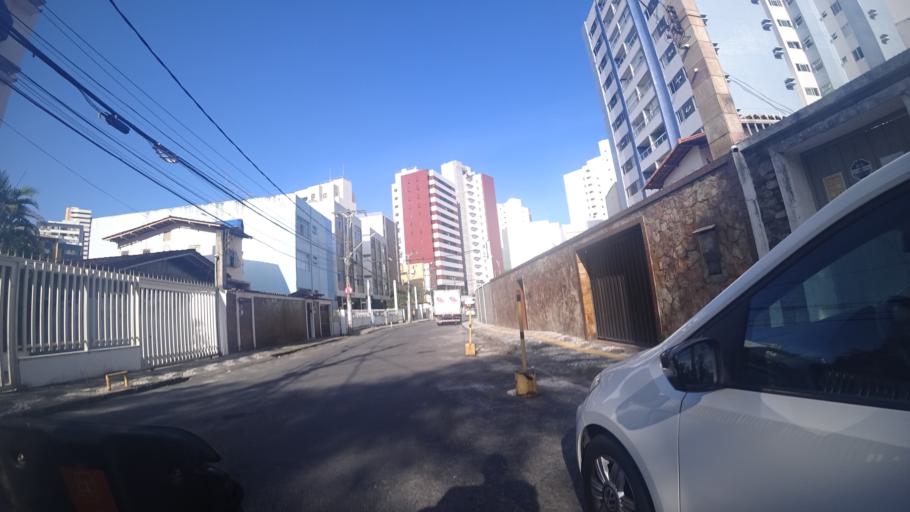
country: BR
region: Bahia
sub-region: Salvador
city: Salvador
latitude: -12.9968
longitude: -38.4532
